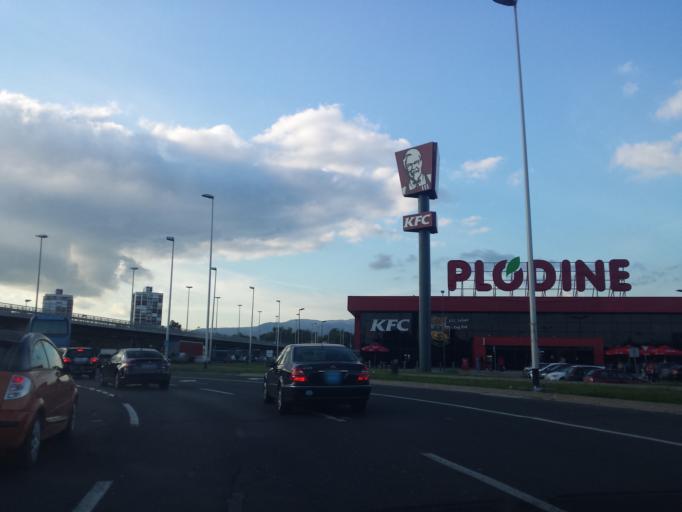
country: HR
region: Grad Zagreb
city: Novi Zagreb
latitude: 45.7783
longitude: 16.0028
